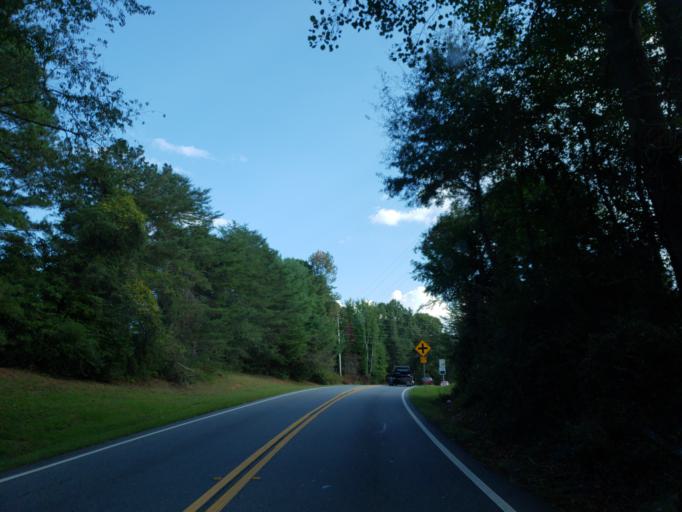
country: US
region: Georgia
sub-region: Fulton County
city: Roswell
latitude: 34.0709
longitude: -84.3515
